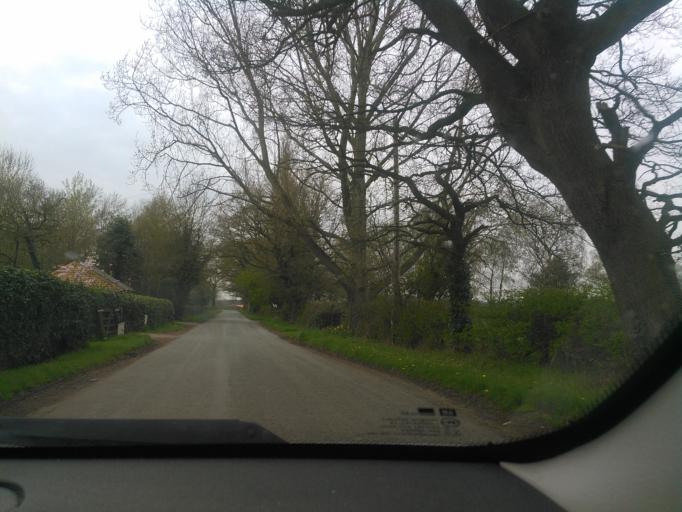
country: GB
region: England
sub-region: Shropshire
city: Shawbury
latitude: 52.8000
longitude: -2.5910
